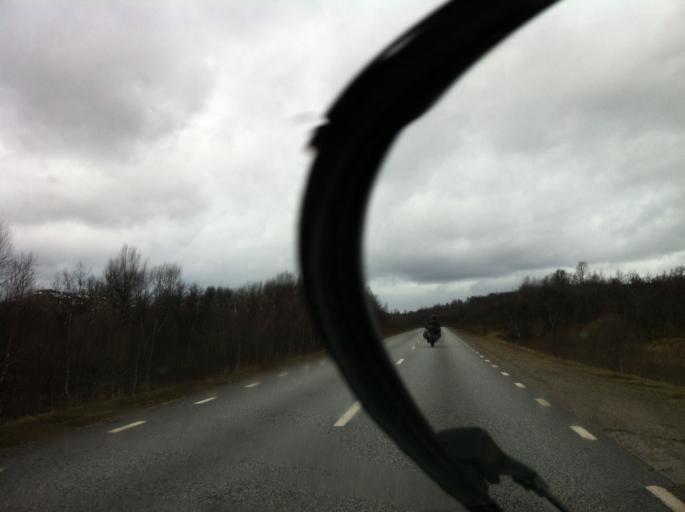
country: NO
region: Sor-Trondelag
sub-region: Tydal
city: Aas
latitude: 62.6106
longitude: 12.1539
